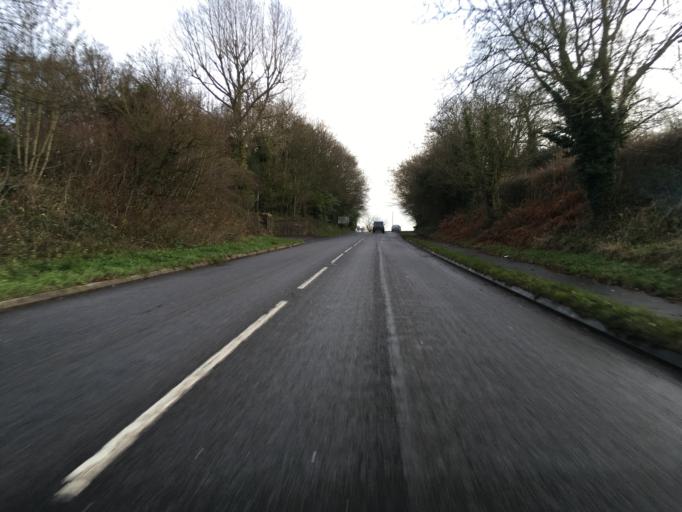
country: GB
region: England
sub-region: South Gloucestershire
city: Almondsbury
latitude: 51.5636
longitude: -2.5583
